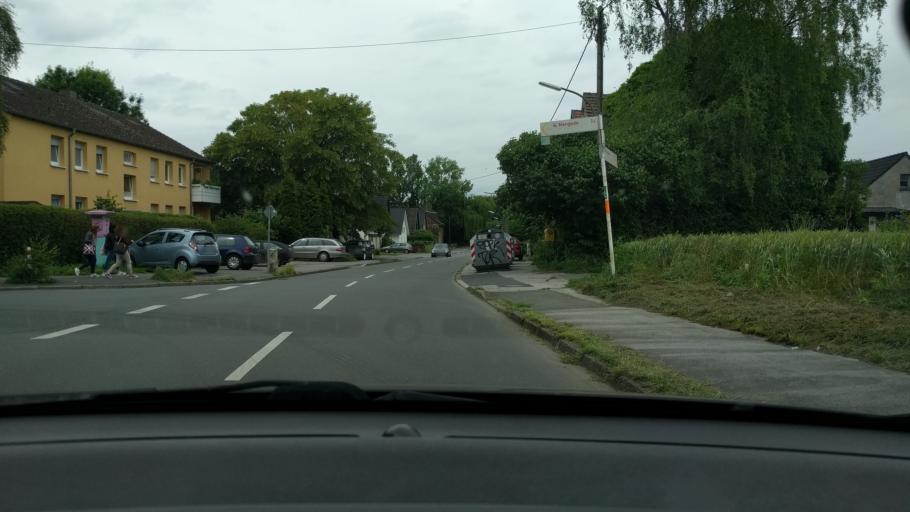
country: DE
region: North Rhine-Westphalia
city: Waltrop
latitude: 51.5822
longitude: 7.4249
